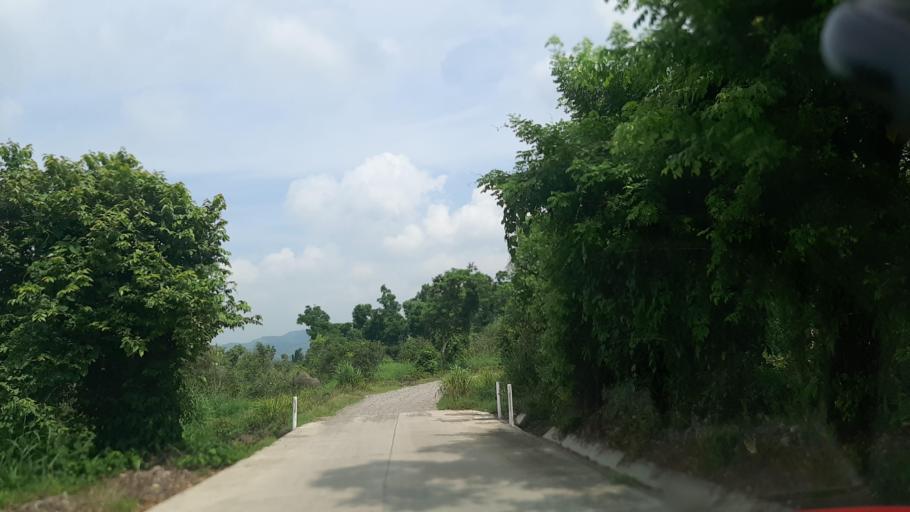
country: MX
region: Veracruz
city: Gutierrez Zamora
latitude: 20.4466
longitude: -97.1754
